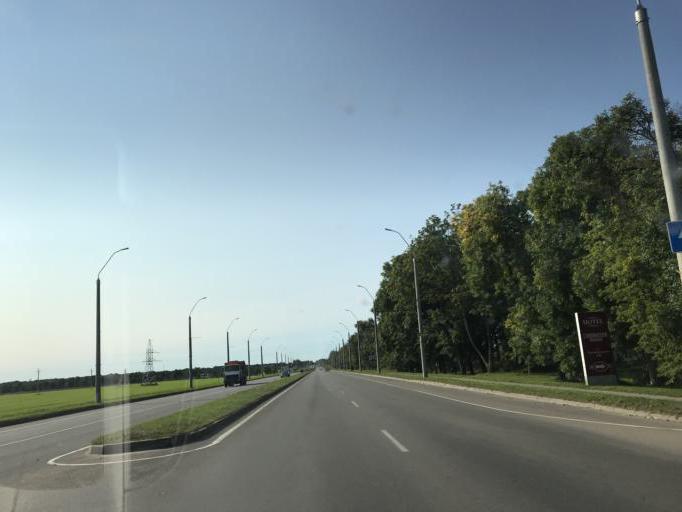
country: BY
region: Mogilev
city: Buynichy
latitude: 53.8756
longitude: 30.2647
